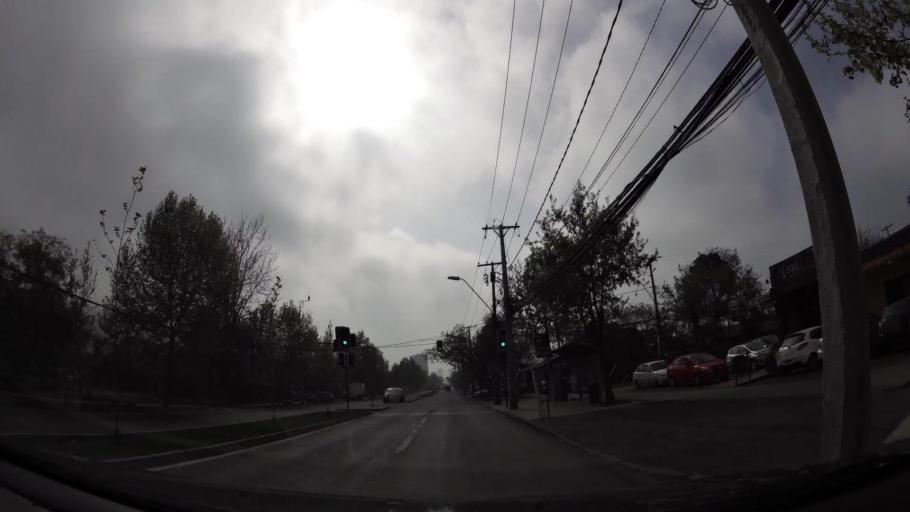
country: CL
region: Santiago Metropolitan
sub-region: Provincia de Santiago
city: Villa Presidente Frei, Nunoa, Santiago, Chile
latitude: -33.3822
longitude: -70.5467
